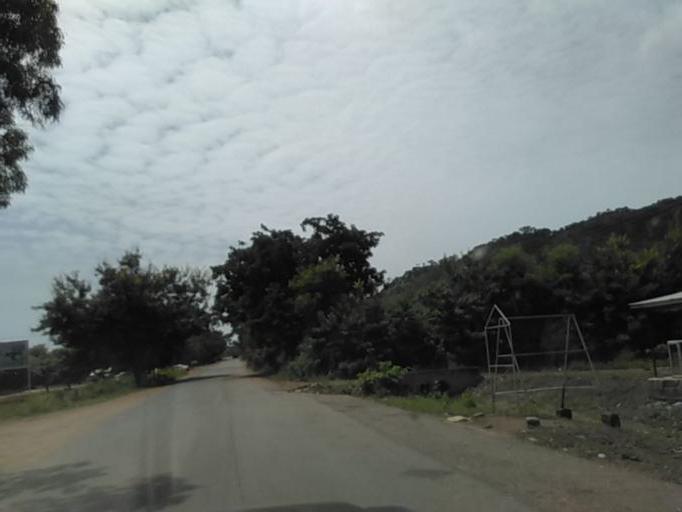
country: GH
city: Akropong
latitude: 6.0936
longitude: 0.0447
